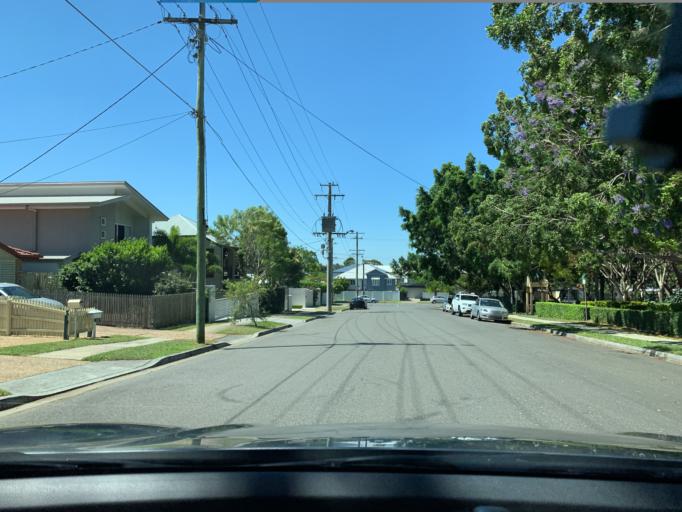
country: AU
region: Queensland
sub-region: Brisbane
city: Ascot
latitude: -27.4195
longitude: 153.0682
